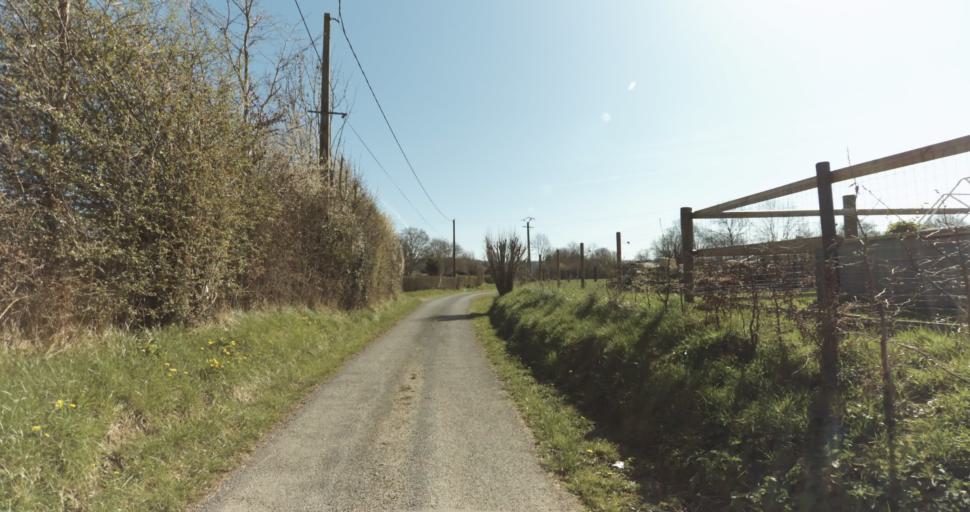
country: FR
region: Lower Normandy
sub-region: Departement du Calvados
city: Saint-Pierre-sur-Dives
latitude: 48.9616
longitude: 0.0534
